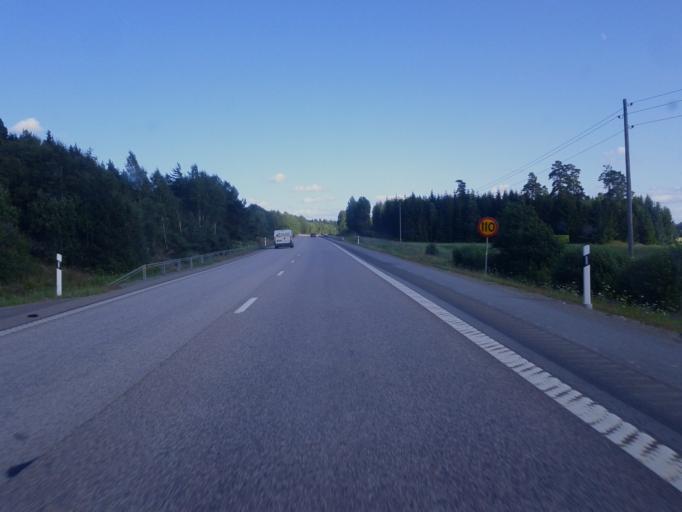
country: SE
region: Uppsala
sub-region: Habo Kommun
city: Balsta
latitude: 59.5554
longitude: 17.5833
